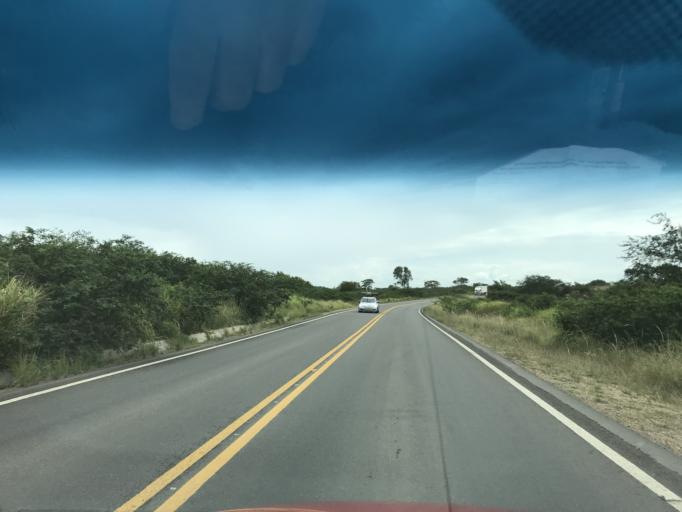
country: BR
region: Bahia
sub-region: Castro Alves
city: Castro Alves
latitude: -12.7500
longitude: -39.4058
